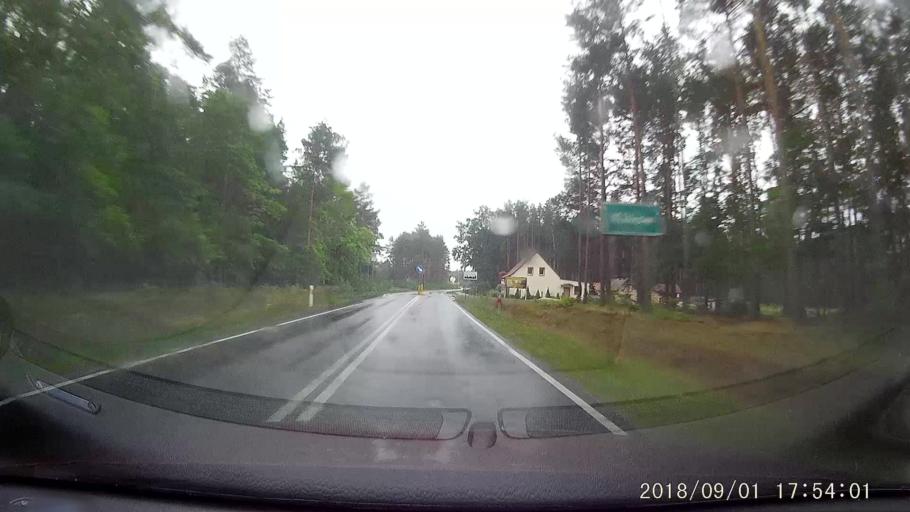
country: PL
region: Lubusz
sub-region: Powiat zaganski
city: Ilowa
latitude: 51.4729
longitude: 15.1993
